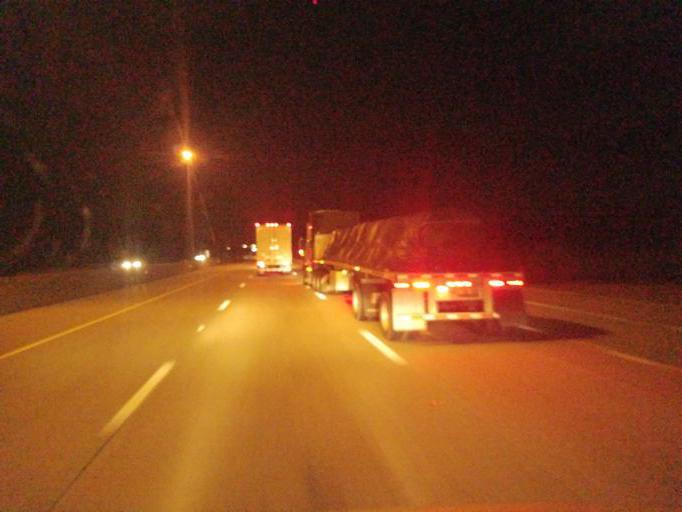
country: US
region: Ohio
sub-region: Montgomery County
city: Huber Heights
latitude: 39.8672
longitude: -84.0945
